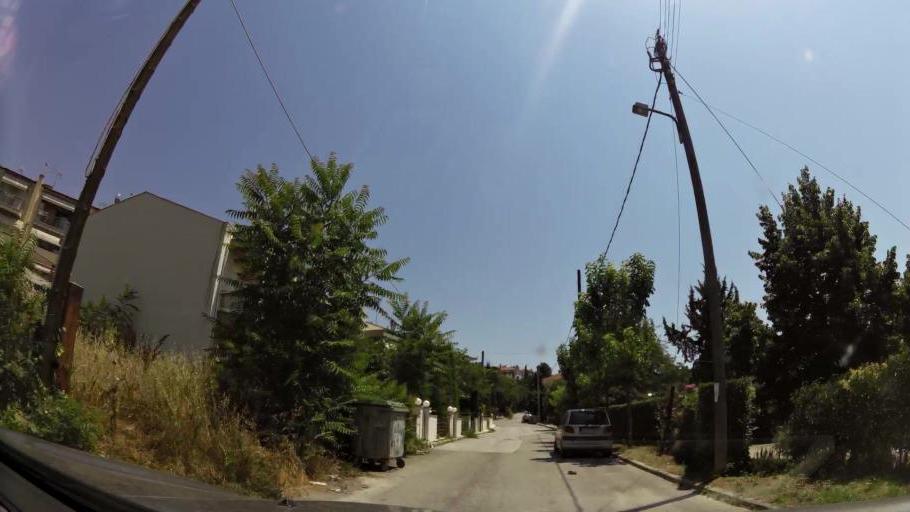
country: GR
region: Central Macedonia
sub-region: Nomos Thessalonikis
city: Trilofos
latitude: 40.4648
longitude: 22.9741
